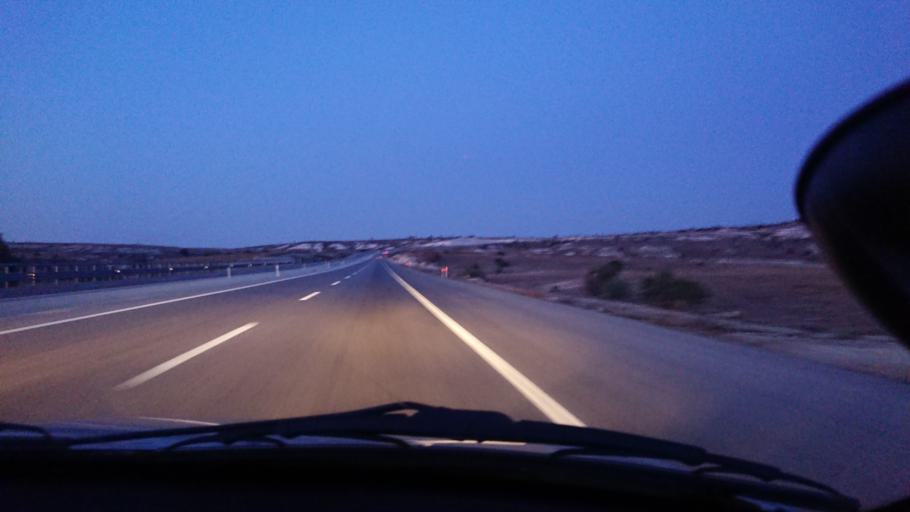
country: TR
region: Kuetahya
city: Cavdarhisar
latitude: 39.1354
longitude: 29.5561
